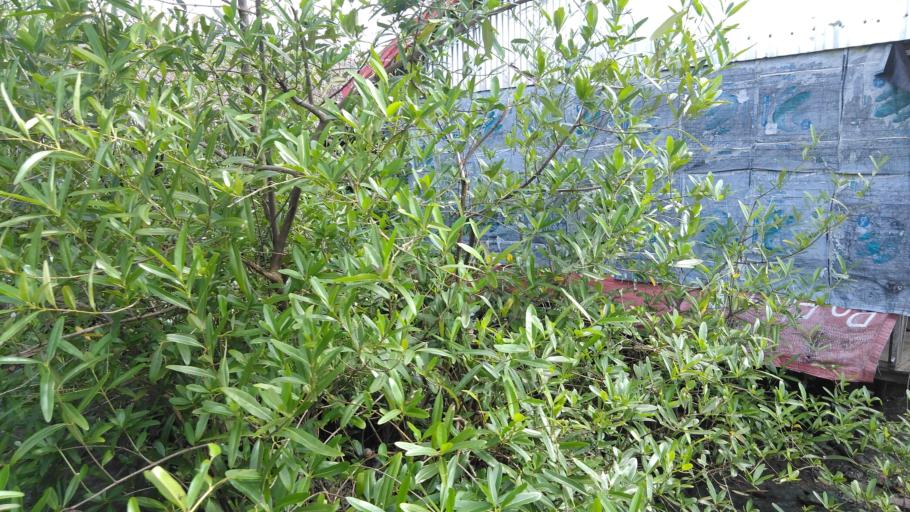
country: NG
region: Ondo
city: Igbekebo
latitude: 5.9256
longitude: 4.9623
